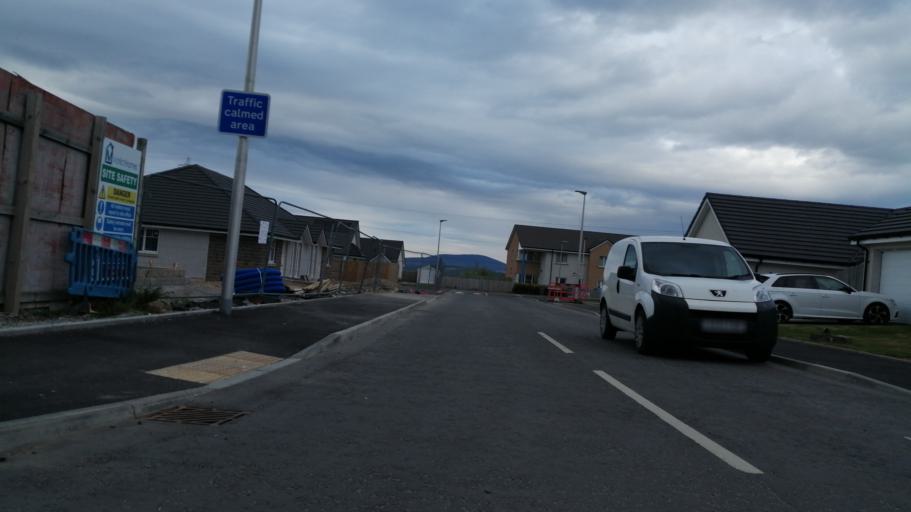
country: GB
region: Scotland
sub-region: Moray
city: Keith
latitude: 57.5352
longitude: -2.9413
